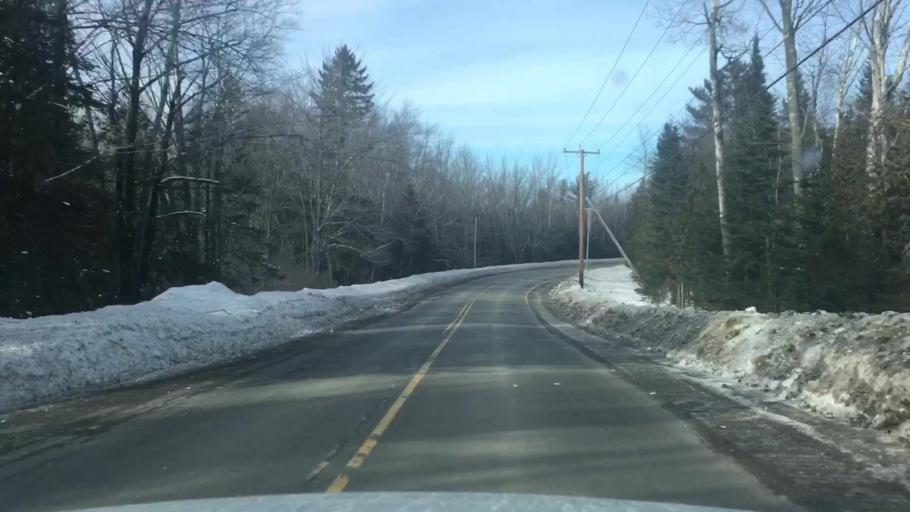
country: US
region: Maine
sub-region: Penobscot County
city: Charleston
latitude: 45.0384
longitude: -69.0332
